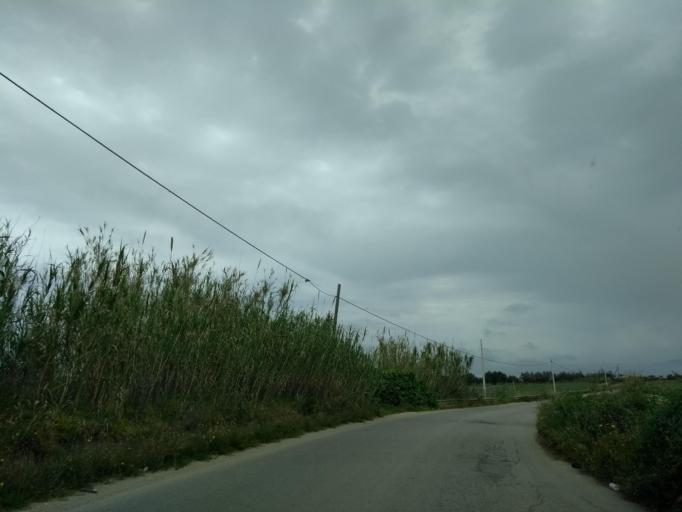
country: IT
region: Sicily
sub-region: Palermo
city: Partinico
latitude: 38.0056
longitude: 13.0679
